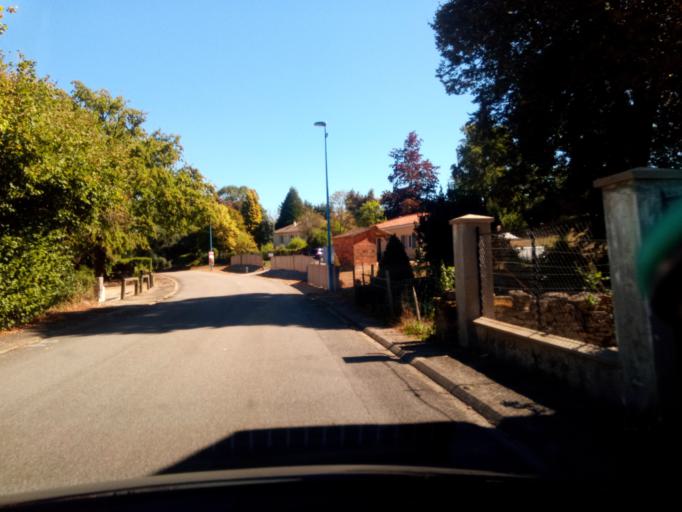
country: FR
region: Limousin
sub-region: Departement de la Haute-Vienne
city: Nantiat
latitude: 46.0777
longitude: 1.2026
